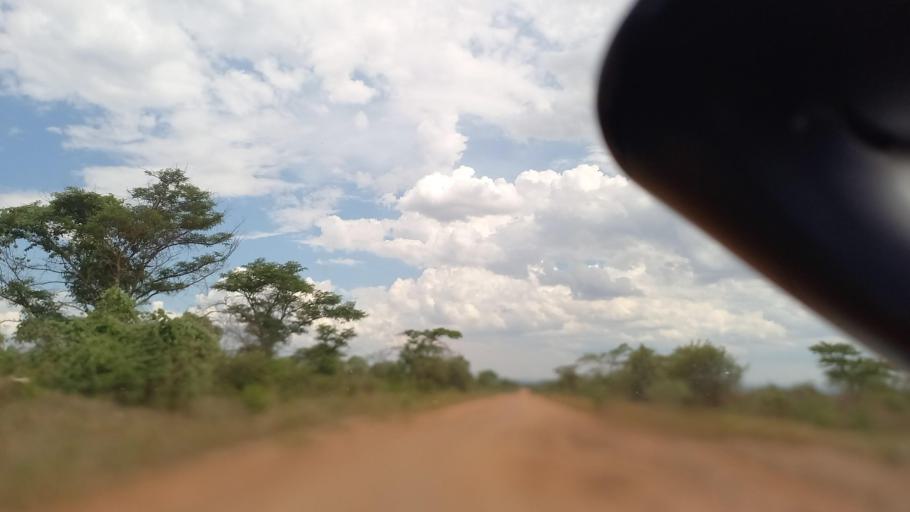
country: ZM
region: Southern
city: Nakambala
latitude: -16.0388
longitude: 27.9722
